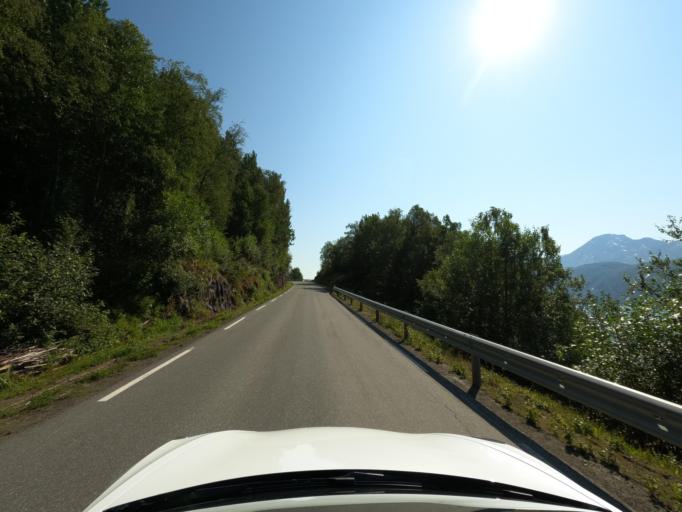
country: NO
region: Nordland
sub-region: Narvik
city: Narvik
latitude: 68.3613
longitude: 17.2630
